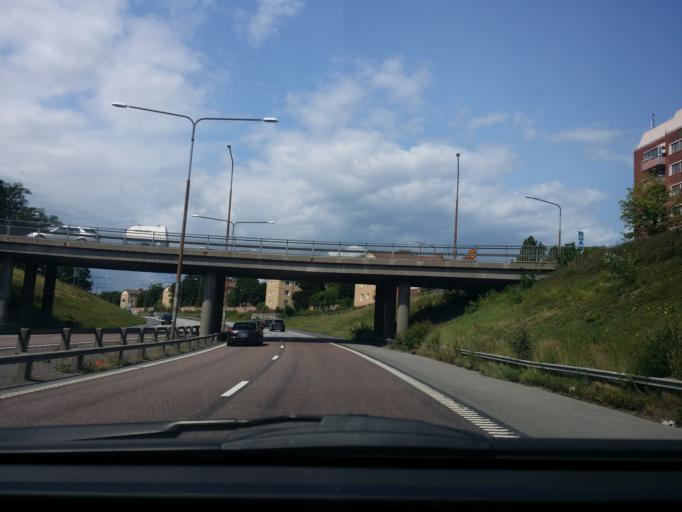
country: SE
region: Vaestmanland
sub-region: Vasteras
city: Vasteras
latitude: 59.6241
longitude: 16.5486
